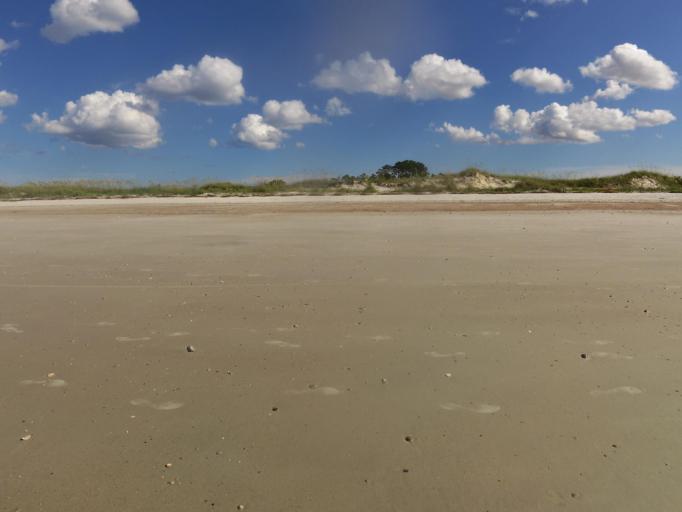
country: US
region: Florida
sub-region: Nassau County
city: Fernandina Beach
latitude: 30.7046
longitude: -81.4370
